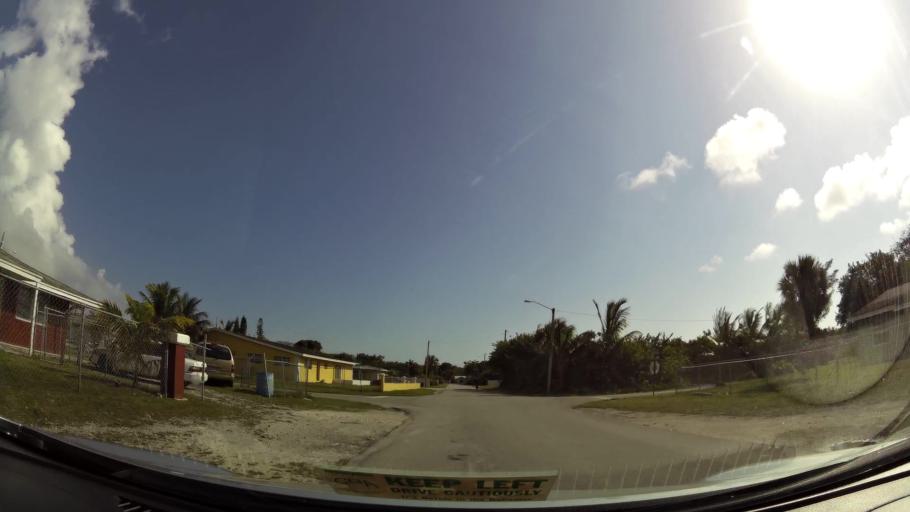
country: BS
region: Freeport
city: Freeport
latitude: 26.5203
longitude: -78.6903
